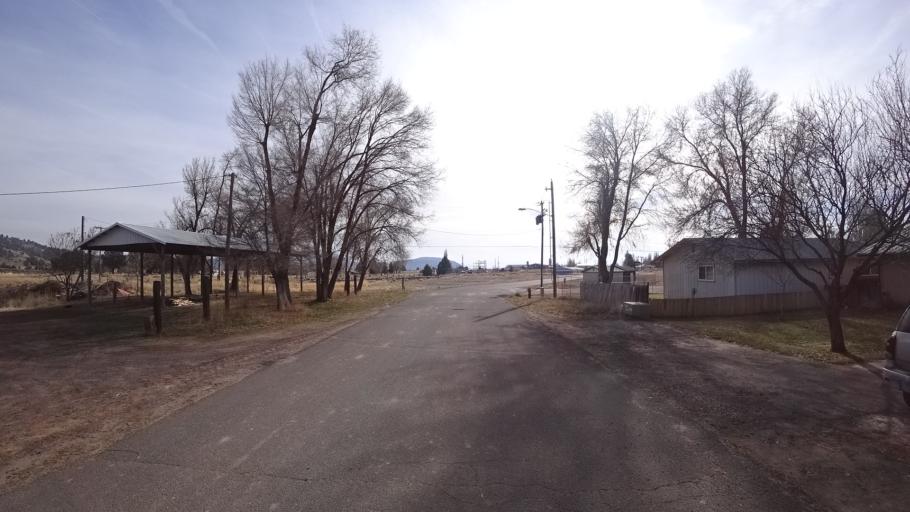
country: US
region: Oregon
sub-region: Klamath County
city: Klamath Falls
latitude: 41.9708
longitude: -121.9131
